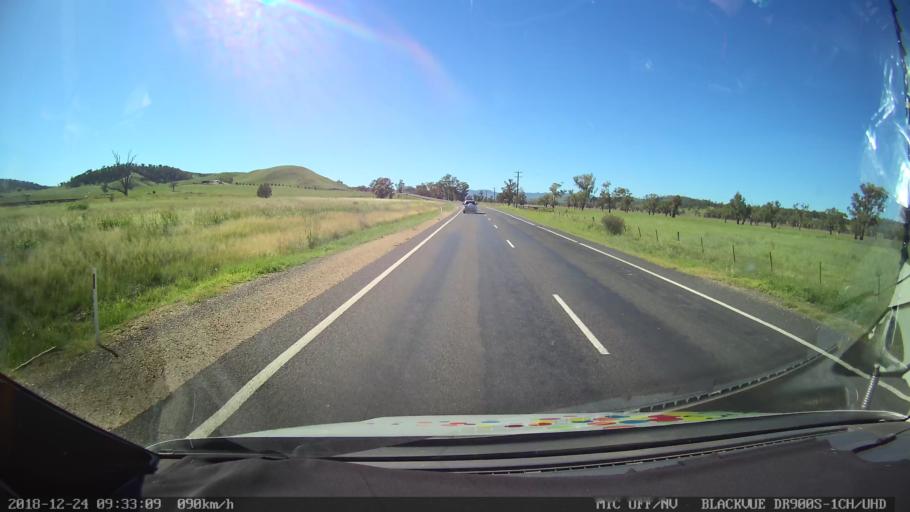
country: AU
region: New South Wales
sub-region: Liverpool Plains
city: Quirindi
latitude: -31.6001
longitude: 150.7057
